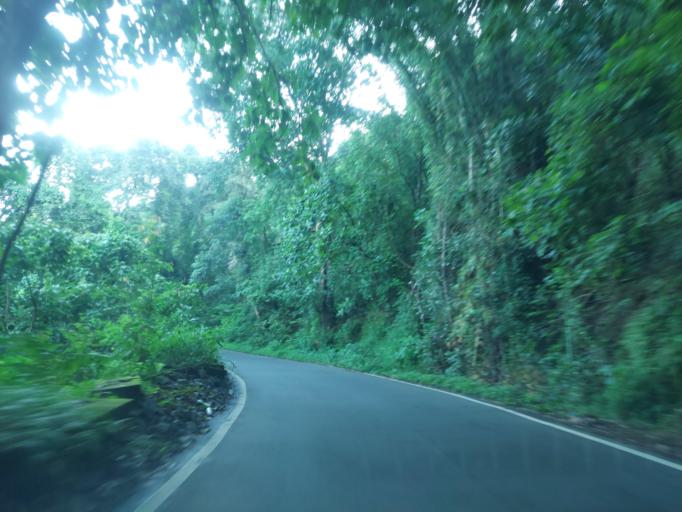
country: IN
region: Maharashtra
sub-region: Sindhudurg
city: Savantvadi
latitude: 15.9347
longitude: 73.9429
